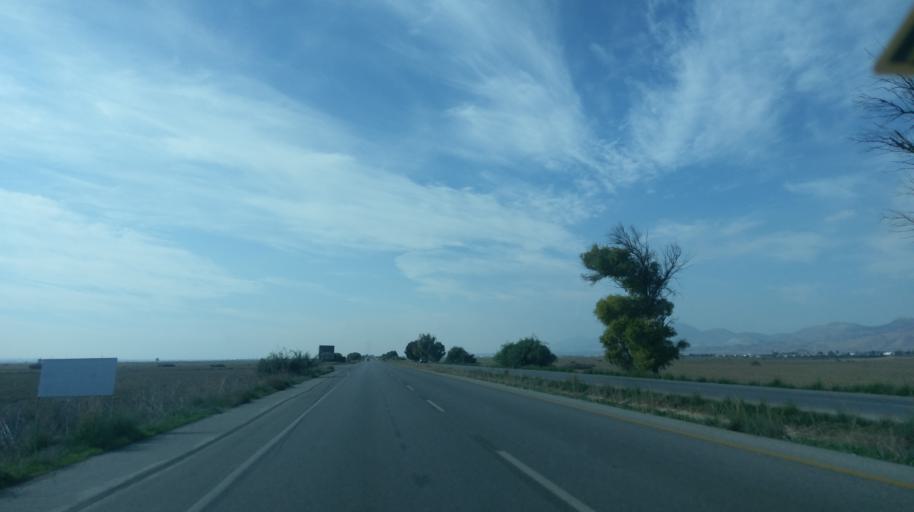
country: CY
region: Larnaka
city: Athienou
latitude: 35.2091
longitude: 33.5771
